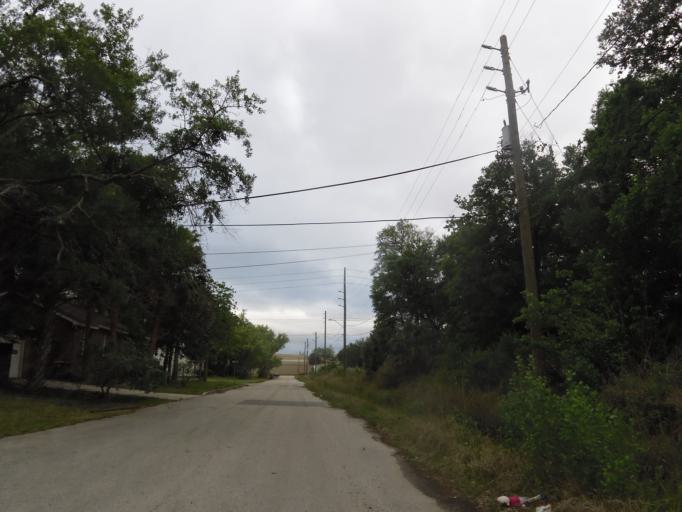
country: US
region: Florida
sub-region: Duval County
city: Jacksonville
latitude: 30.3132
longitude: -81.6471
